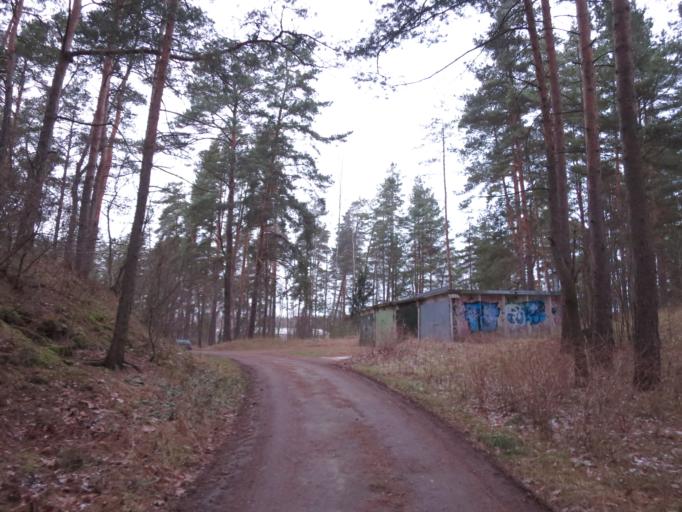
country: LV
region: Riga
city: Bergi
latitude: 56.9759
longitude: 24.3123
